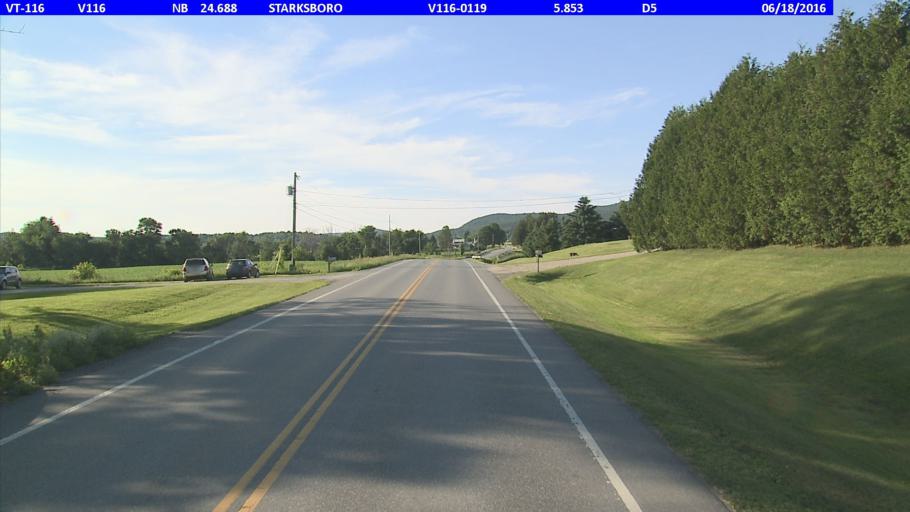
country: US
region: Vermont
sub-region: Chittenden County
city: Hinesburg
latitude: 44.2683
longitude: -73.0673
